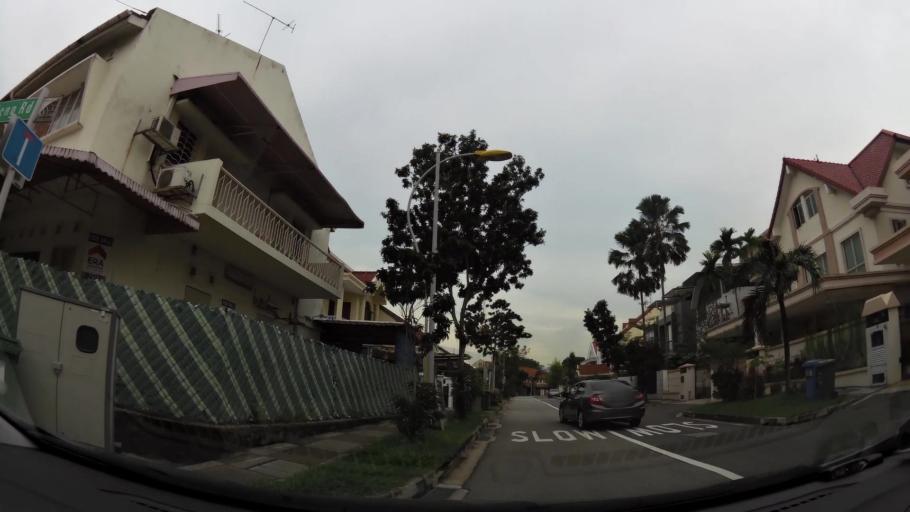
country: SG
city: Singapore
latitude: 1.3326
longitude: 103.8718
